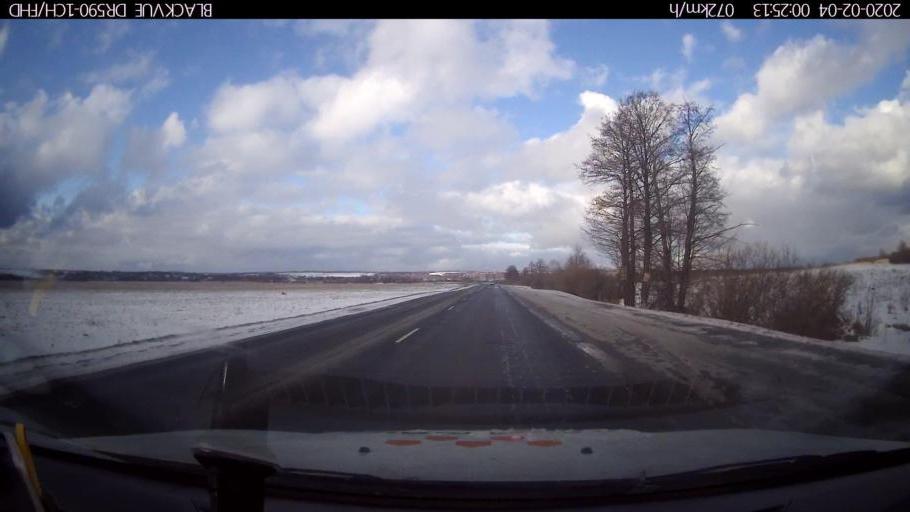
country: RU
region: Nizjnij Novgorod
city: Kstovo
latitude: 56.0035
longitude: 44.2104
